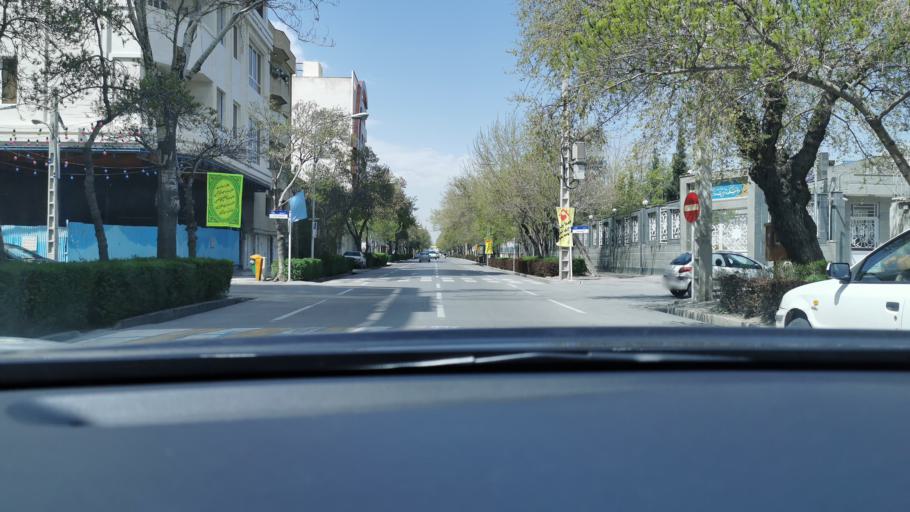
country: IR
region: Razavi Khorasan
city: Mashhad
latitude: 36.2995
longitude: 59.5887
